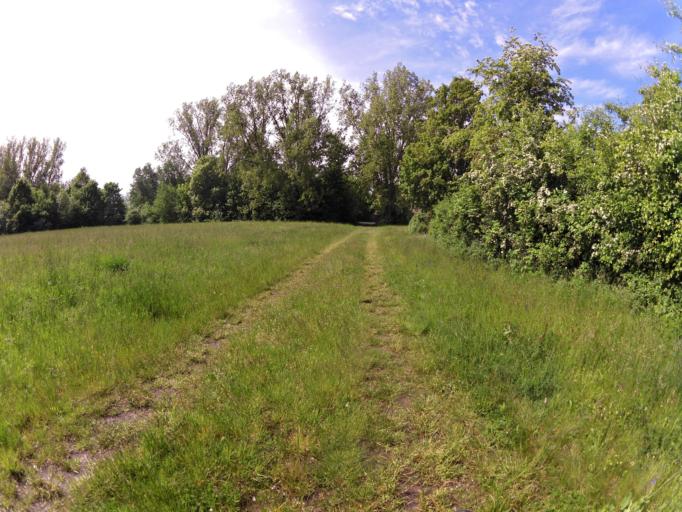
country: DE
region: Bavaria
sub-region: Regierungsbezirk Unterfranken
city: Volkach
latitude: 49.8608
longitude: 10.2209
